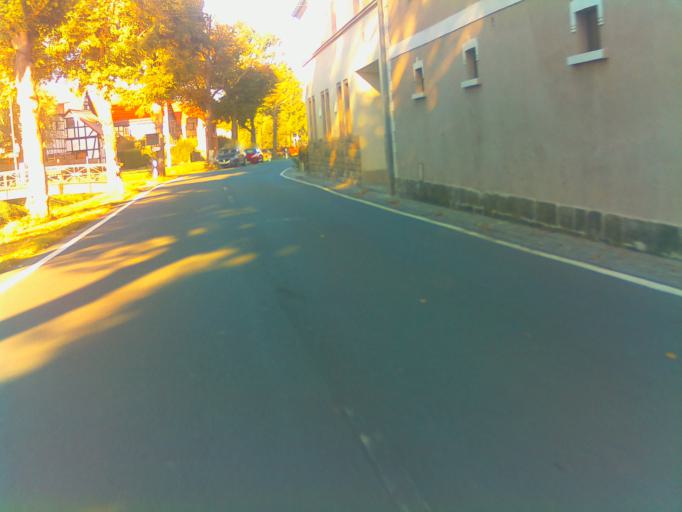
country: DE
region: Thuringia
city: Ottendorf
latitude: 50.8273
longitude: 11.7995
